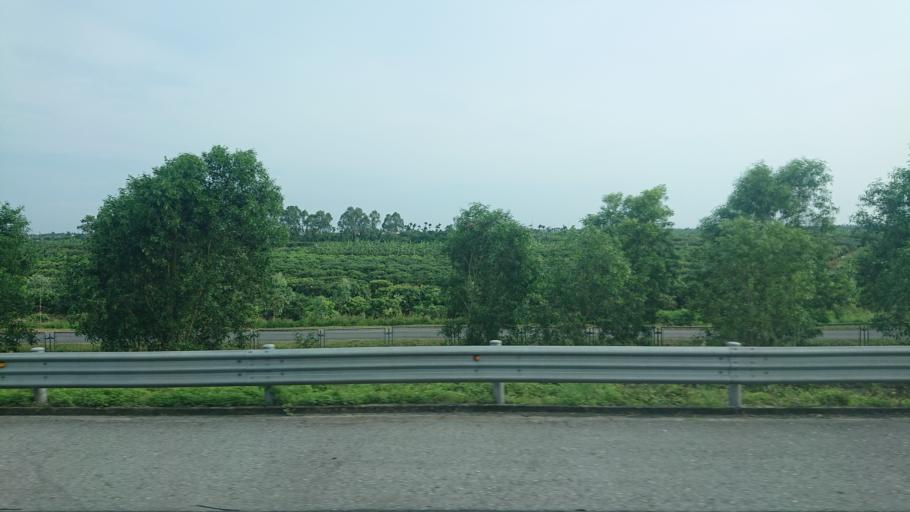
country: VN
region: Hai Phong
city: An Lao
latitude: 20.8192
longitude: 106.4815
